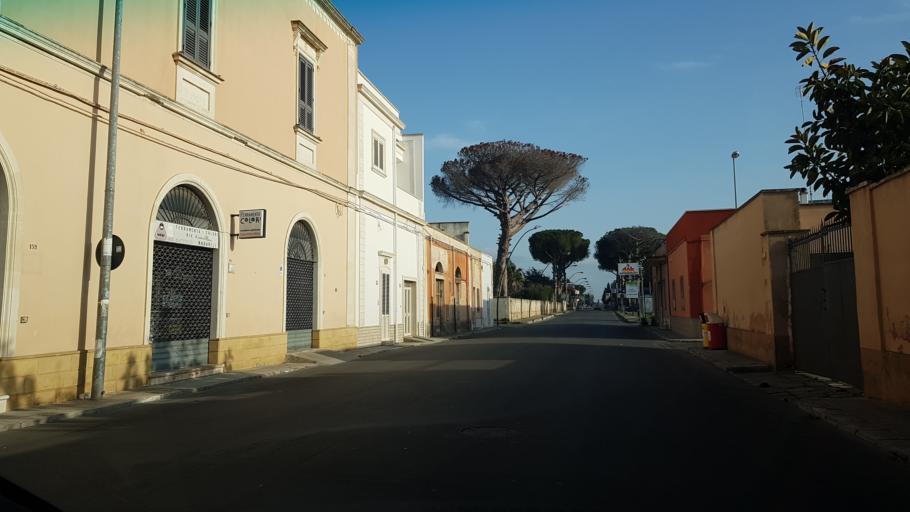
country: IT
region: Apulia
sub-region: Provincia di Lecce
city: Squinzano
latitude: 40.4332
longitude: 18.0486
